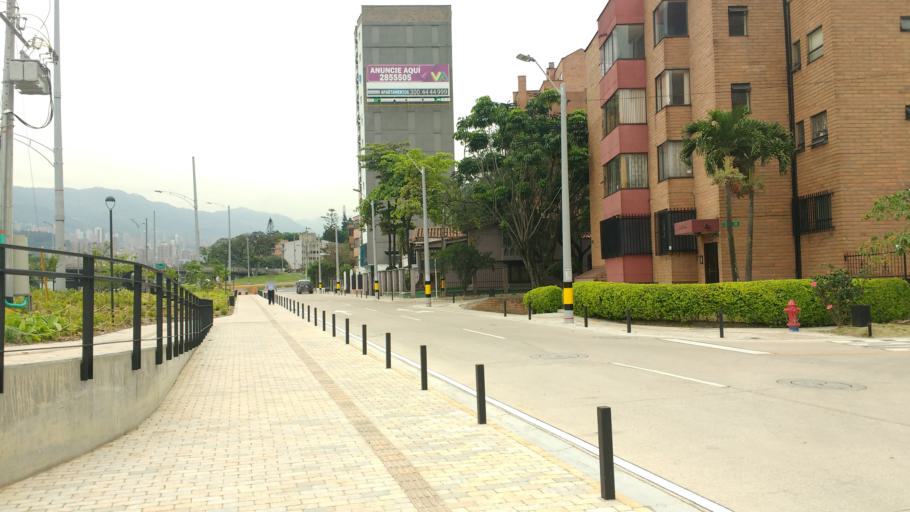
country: CO
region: Antioquia
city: Medellin
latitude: 6.2415
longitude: -75.5788
